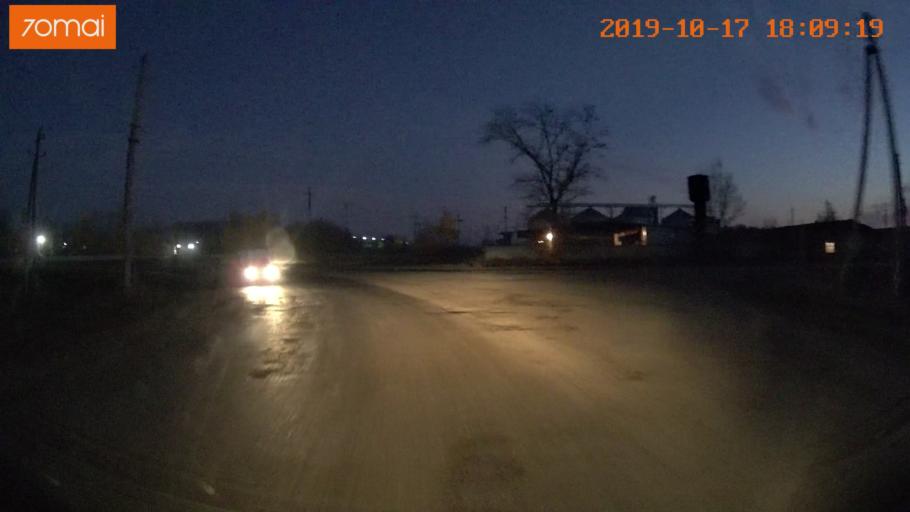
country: RU
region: Tula
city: Kurkino
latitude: 53.4247
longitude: 38.6445
